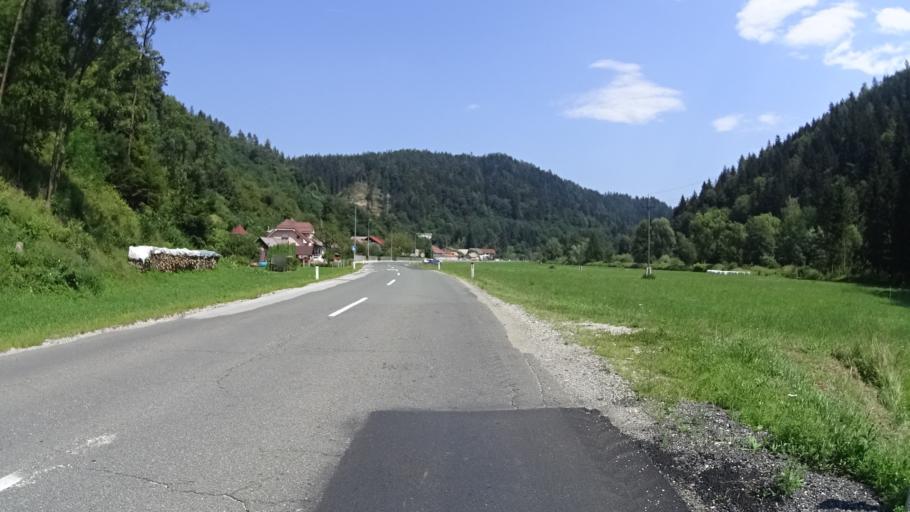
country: SI
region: Prevalje
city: Prevalje
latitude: 46.5473
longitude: 14.8872
